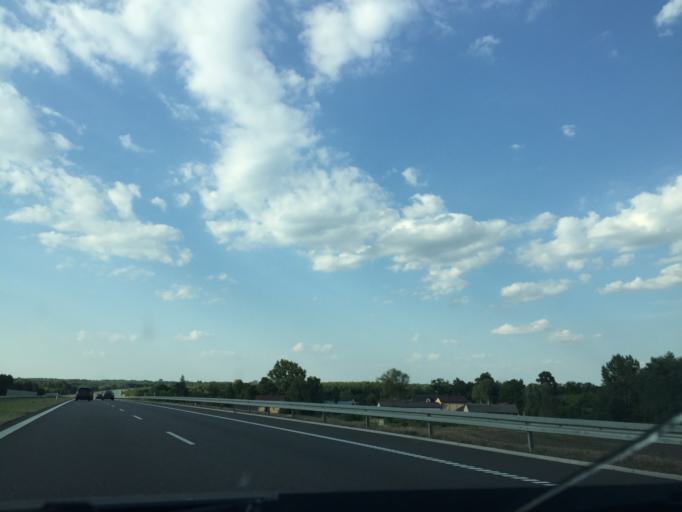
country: PL
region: Masovian Voivodeship
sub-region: Powiat radomski
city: Wolanow
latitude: 51.3537
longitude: 21.0143
